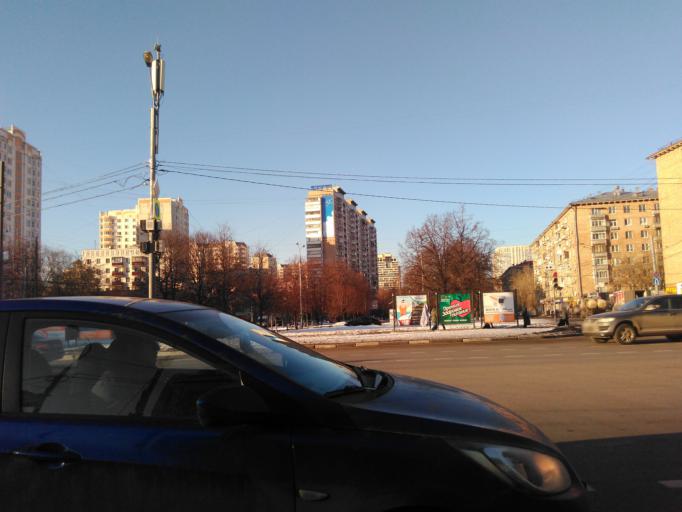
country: RU
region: Moskovskaya
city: Cheremushki
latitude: 55.6780
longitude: 37.5631
